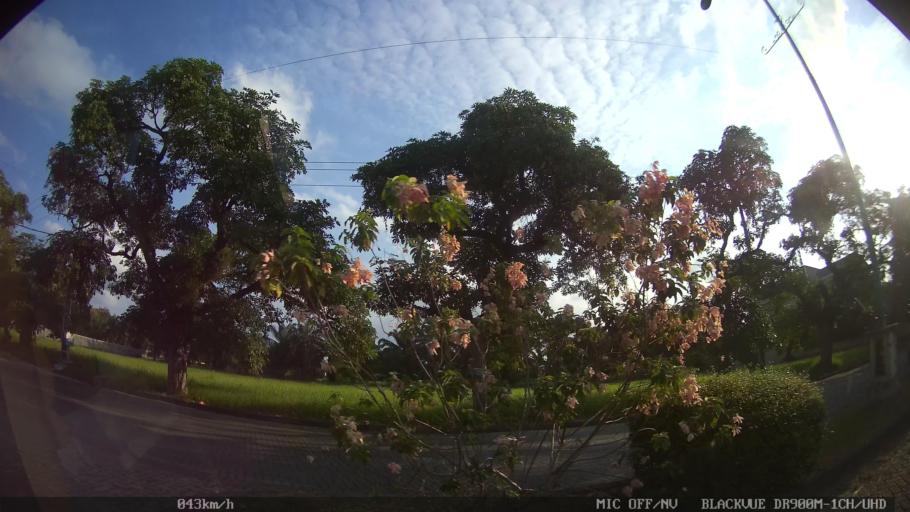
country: ID
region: North Sumatra
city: Medan
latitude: 3.6252
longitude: 98.6512
